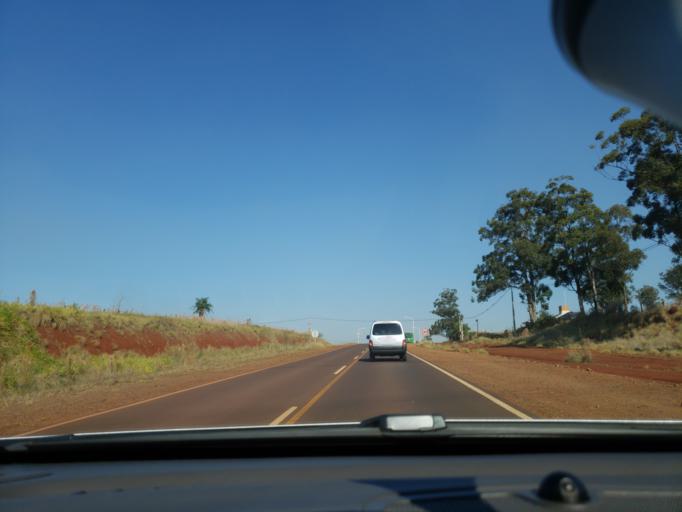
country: AR
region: Misiones
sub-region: Departamento de Capital
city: Posadas
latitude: -27.4618
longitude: -55.9707
